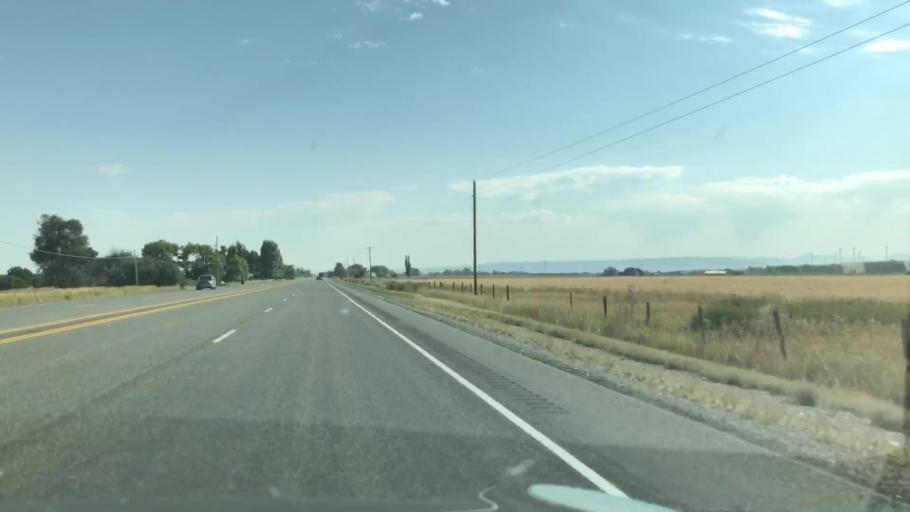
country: US
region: Idaho
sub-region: Bonneville County
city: Iona
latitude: 43.5709
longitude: -111.9135
